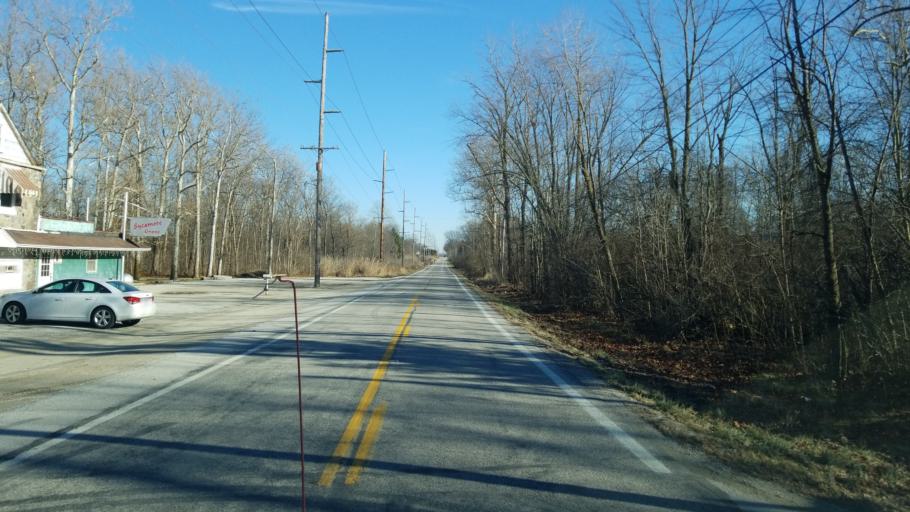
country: US
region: Ohio
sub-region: Wood County
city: Pemberville
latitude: 41.4500
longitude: -83.4345
